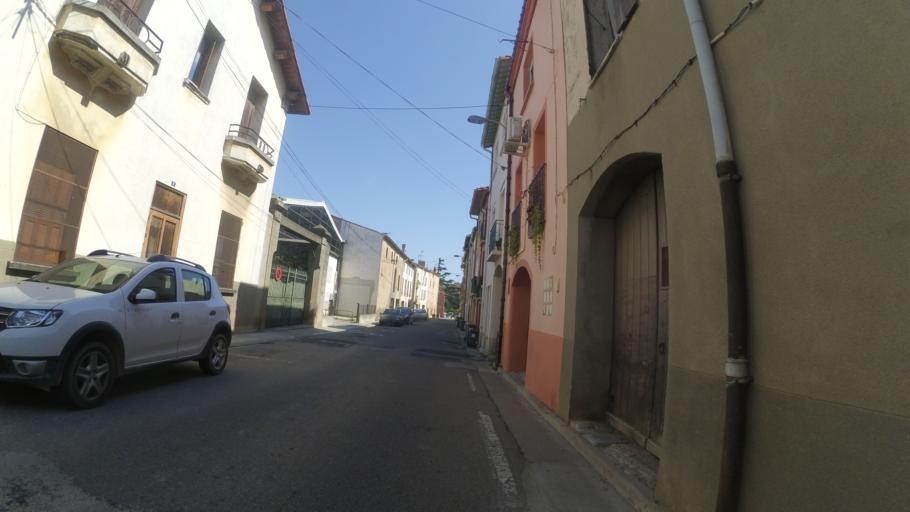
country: FR
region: Languedoc-Roussillon
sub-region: Departement des Pyrenees-Orientales
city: Thuir
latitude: 42.6337
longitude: 2.7538
